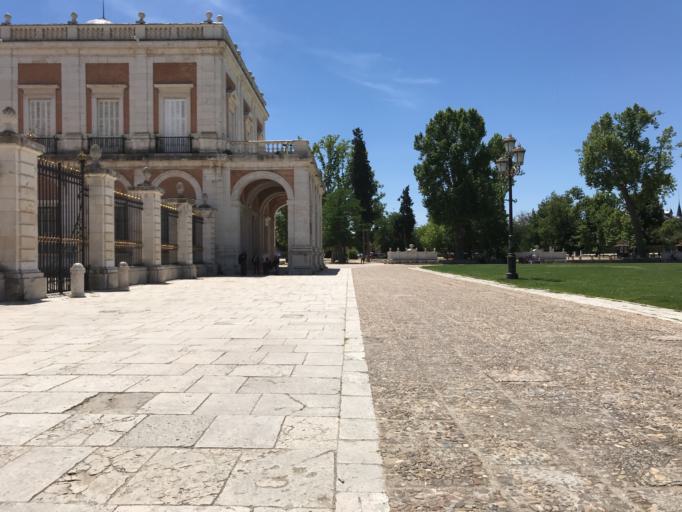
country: ES
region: Madrid
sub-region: Provincia de Madrid
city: Aranjuez
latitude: 40.0364
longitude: -3.6095
